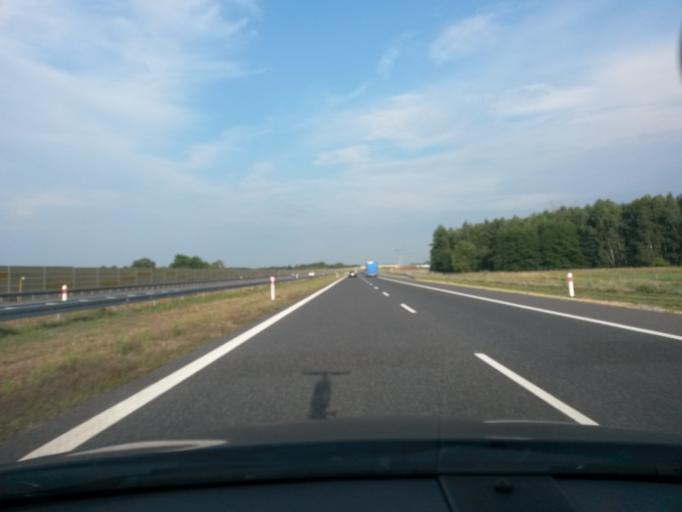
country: PL
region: Lodz Voivodeship
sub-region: Powiat zgierski
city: Ozorkow
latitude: 51.9283
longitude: 19.3068
